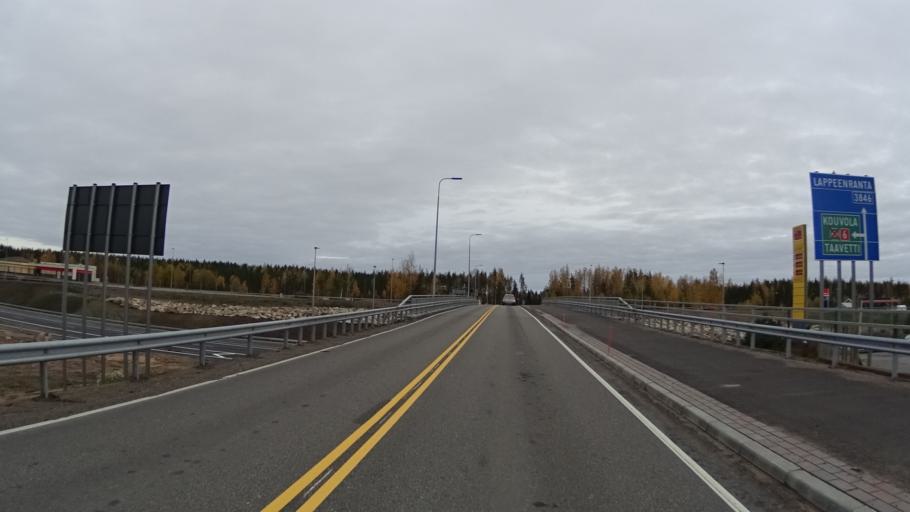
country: FI
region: South Karelia
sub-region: Lappeenranta
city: Luumaeki
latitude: 60.9281
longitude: 27.6310
